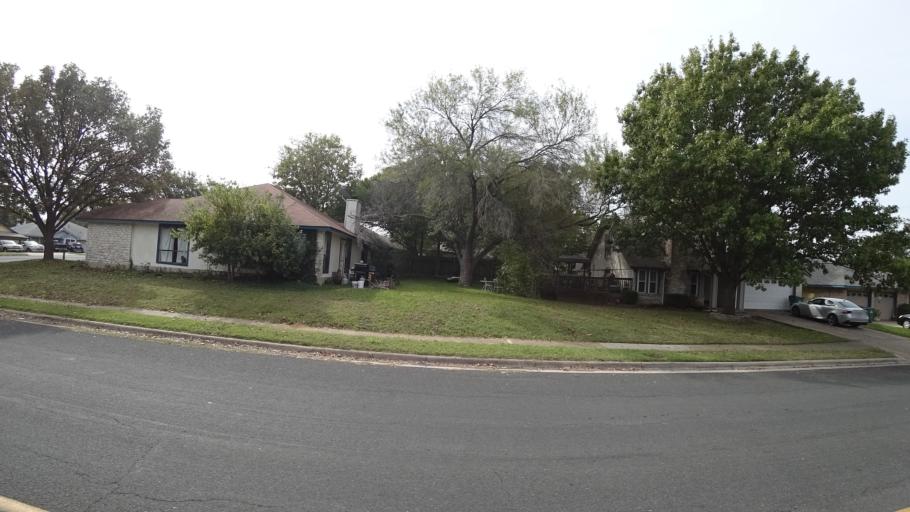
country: US
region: Texas
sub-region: Travis County
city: Wells Branch
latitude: 30.4423
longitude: -97.6810
